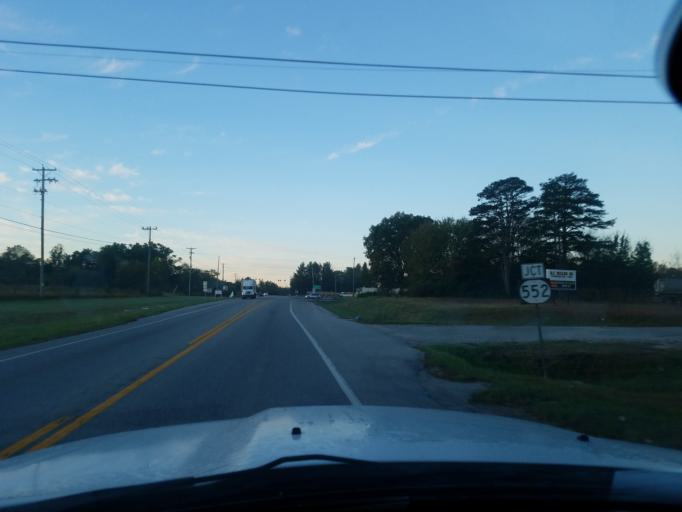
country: US
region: Kentucky
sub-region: Laurel County
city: North Corbin
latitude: 37.0324
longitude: -84.0616
